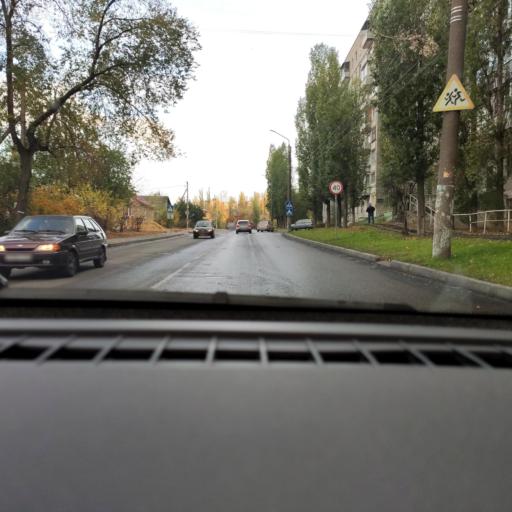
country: RU
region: Voronezj
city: Pridonskoy
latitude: 51.6582
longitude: 39.1163
